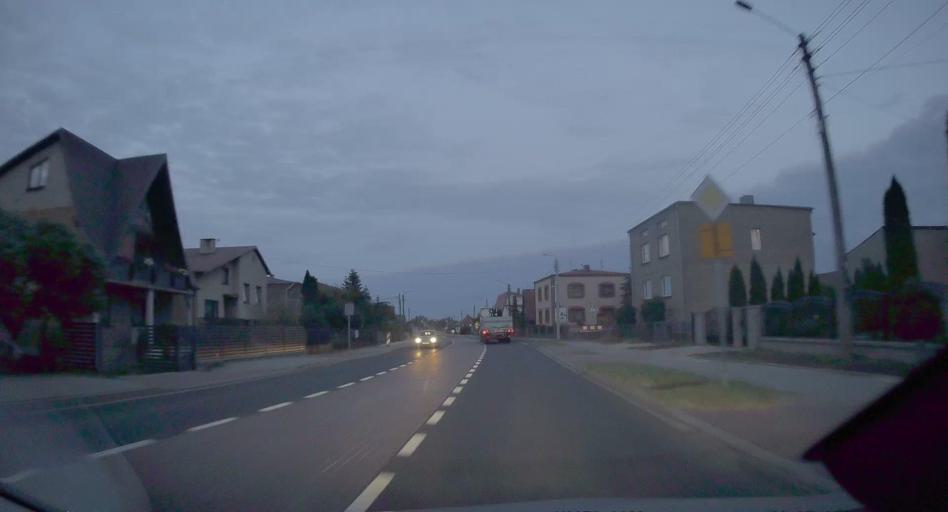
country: PL
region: Silesian Voivodeship
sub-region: Powiat klobucki
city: Opatow
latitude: 50.9278
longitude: 18.8640
